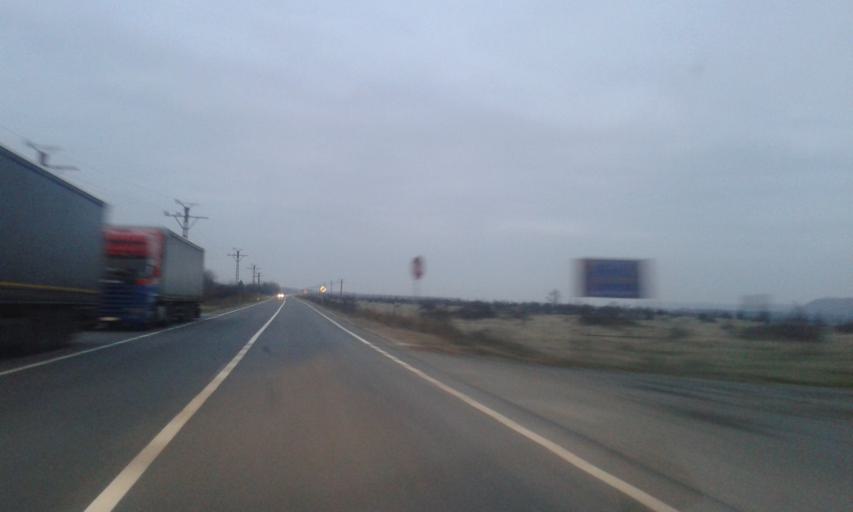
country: RO
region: Gorj
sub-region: Comuna Bumbesti-Jiu
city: Bumbesti-Jiu
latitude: 45.1555
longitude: 23.3744
